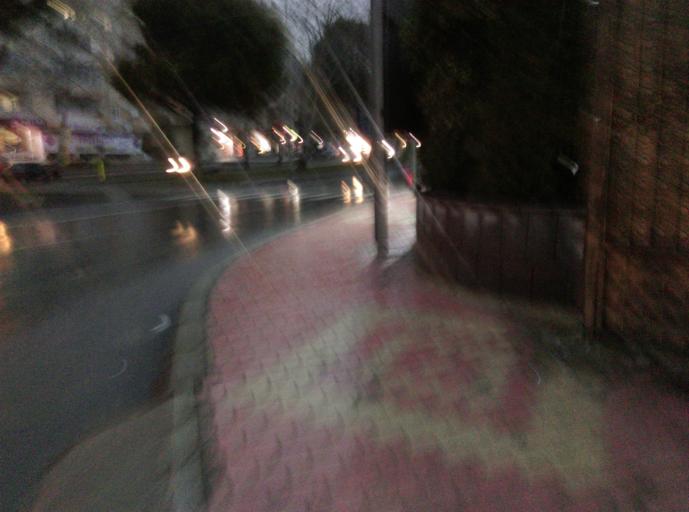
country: TR
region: Kahramanmaras
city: Kahramanmaras
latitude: 37.5845
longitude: 36.8972
